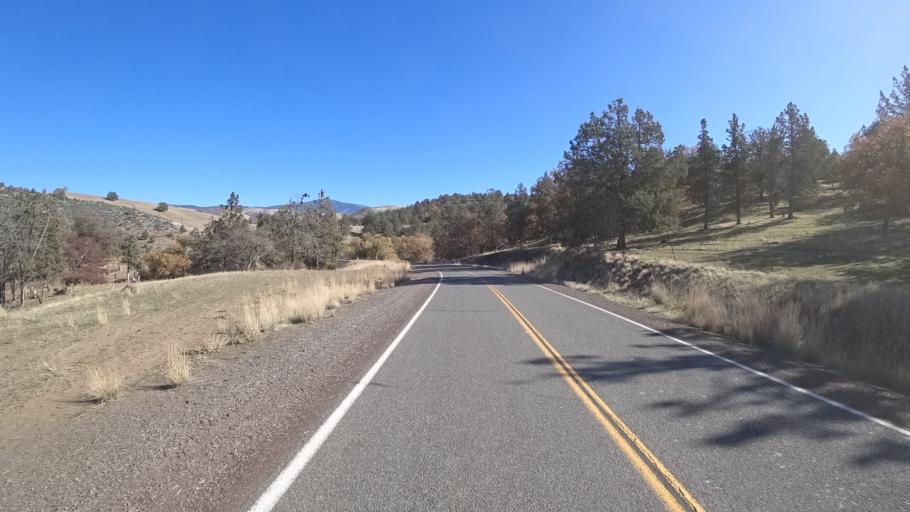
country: US
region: California
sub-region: Siskiyou County
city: Montague
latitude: 41.8074
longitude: -122.3852
